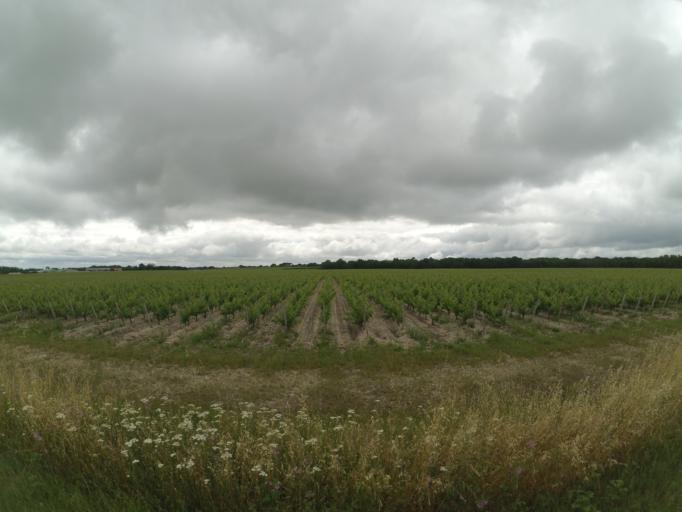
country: FR
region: Aquitaine
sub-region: Departement de la Gironde
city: Lamarque
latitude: 45.0776
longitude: -0.7270
